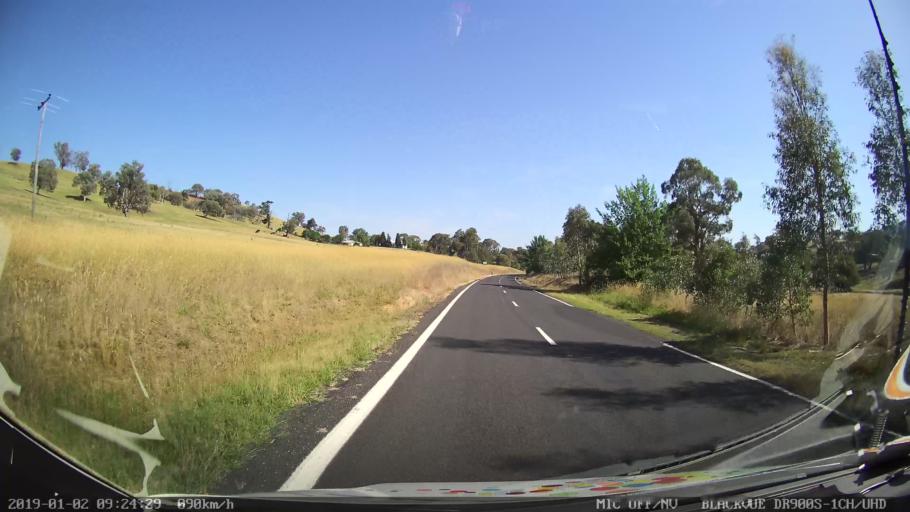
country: AU
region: New South Wales
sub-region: Tumut Shire
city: Tumut
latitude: -35.3764
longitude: 148.2918
